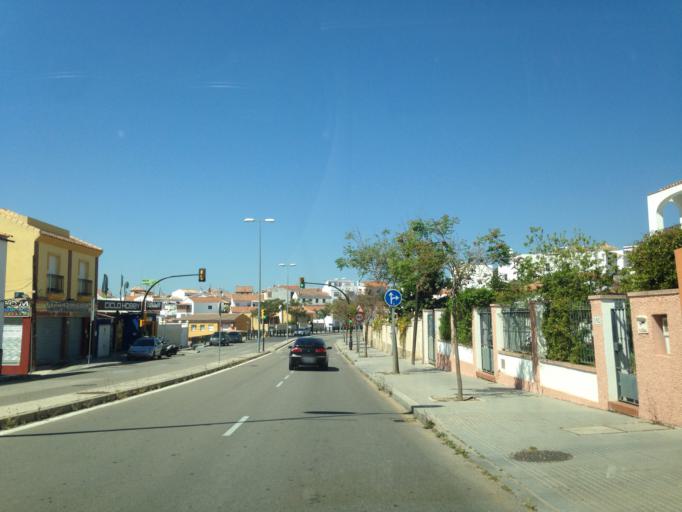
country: ES
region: Andalusia
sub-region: Provincia de Malaga
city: Malaga
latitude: 36.7400
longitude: -4.4849
